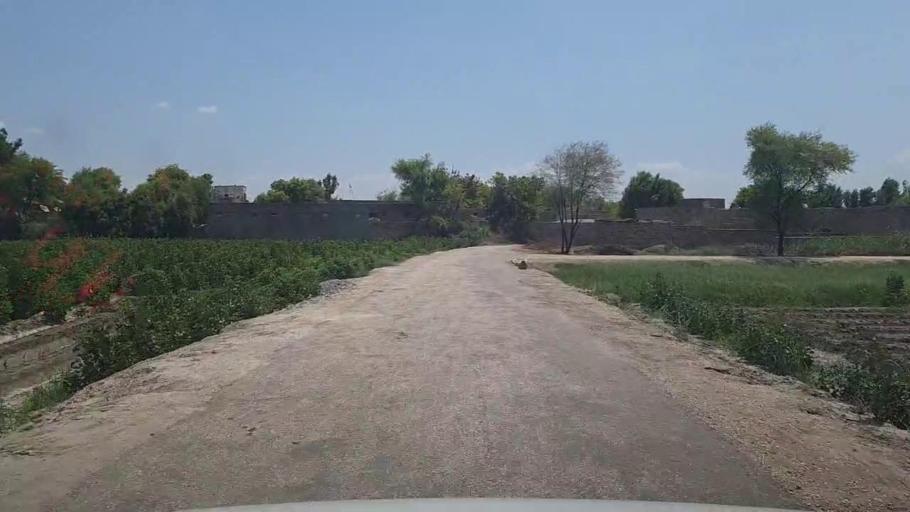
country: PK
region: Sindh
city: Ubauro
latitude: 28.1562
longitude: 69.7496
